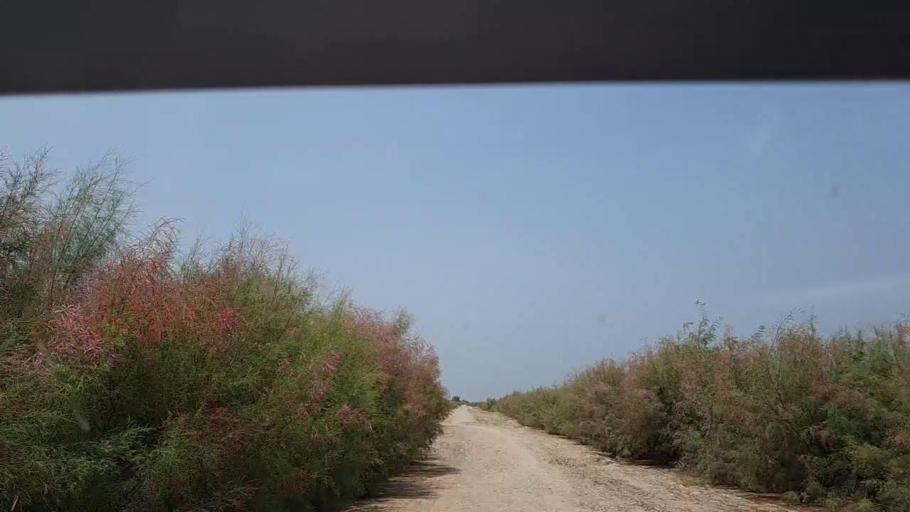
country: PK
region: Sindh
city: Adilpur
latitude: 27.8968
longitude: 69.2394
